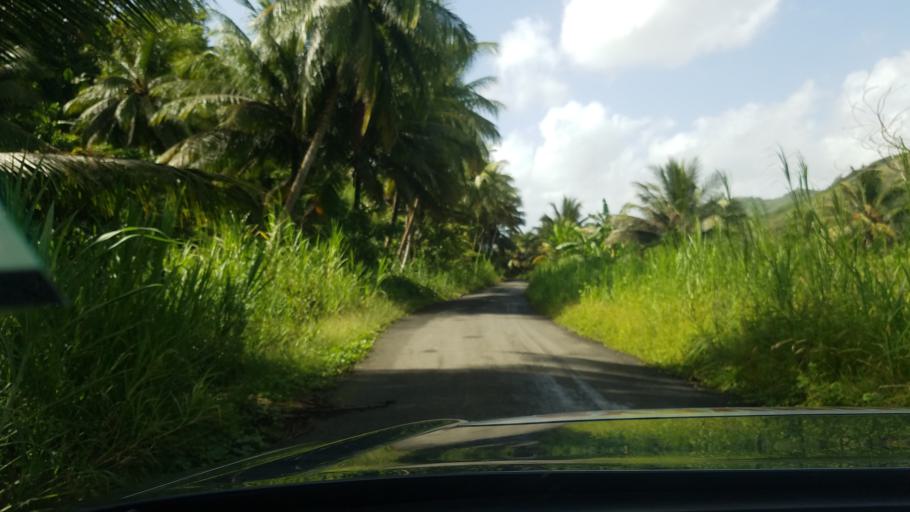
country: LC
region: Anse-la-Raye
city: Anse La Raye
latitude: 13.9531
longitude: -61.0018
